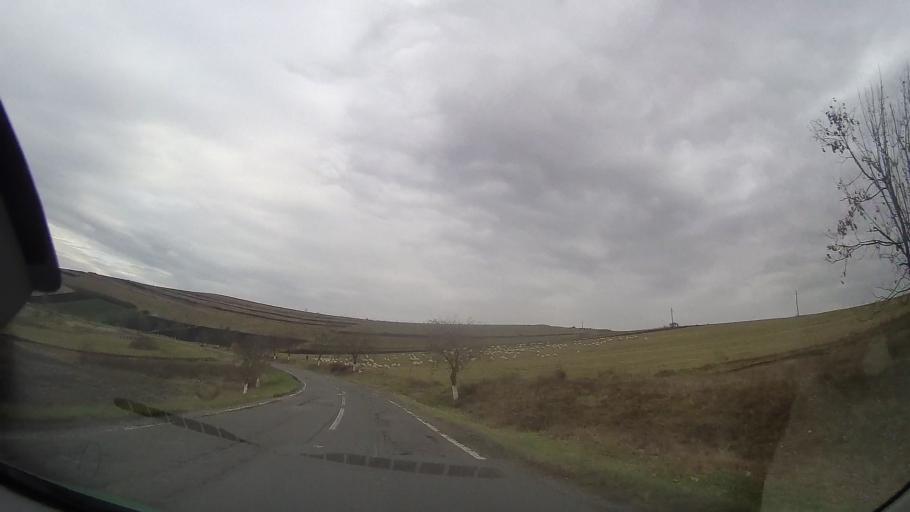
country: RO
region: Mures
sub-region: Comuna Faragau
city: Faragau
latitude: 46.7570
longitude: 24.5360
